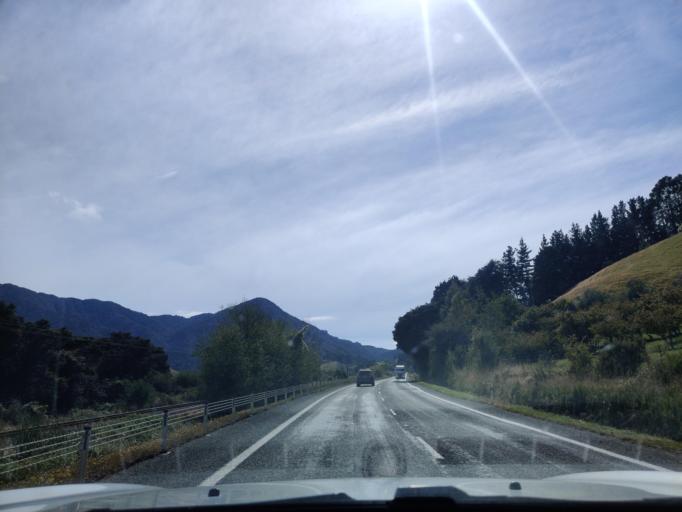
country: NZ
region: Marlborough
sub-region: Marlborough District
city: Picton
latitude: -41.3322
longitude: 173.9677
